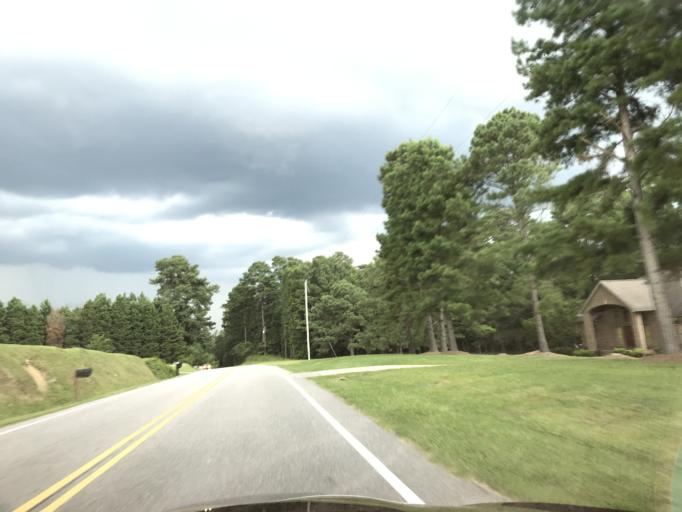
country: US
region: North Carolina
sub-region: Johnston County
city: Four Oaks
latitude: 35.5131
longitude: -78.4723
